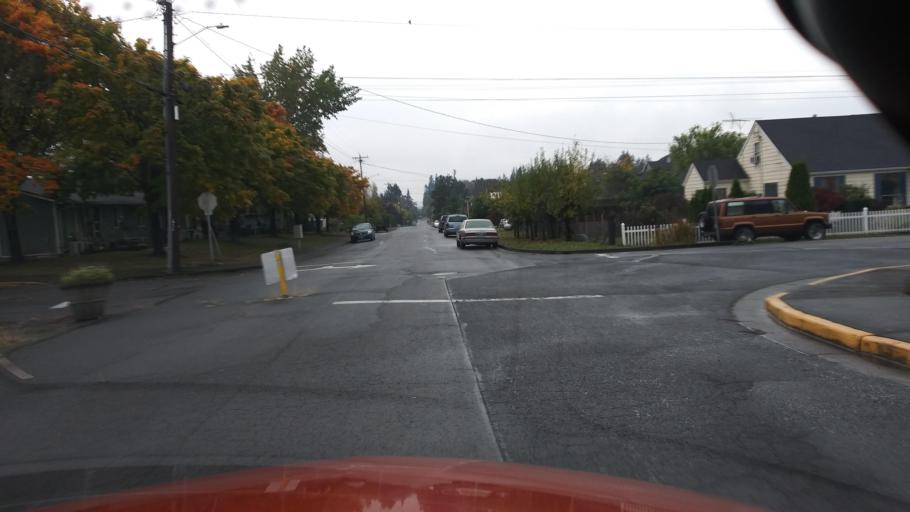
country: US
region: Oregon
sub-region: Washington County
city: North Plains
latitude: 45.5973
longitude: -123.0009
